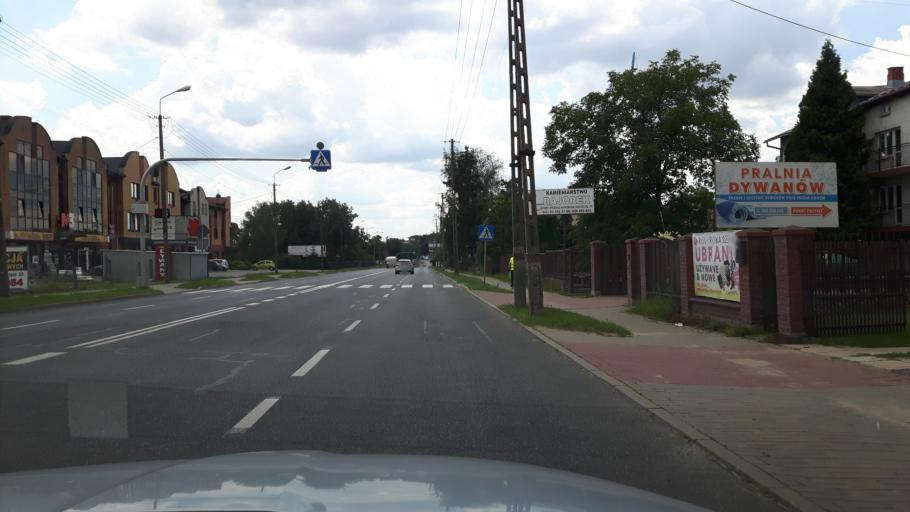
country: PL
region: Masovian Voivodeship
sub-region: Powiat wyszkowski
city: Wyszkow
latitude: 52.5968
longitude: 21.4618
